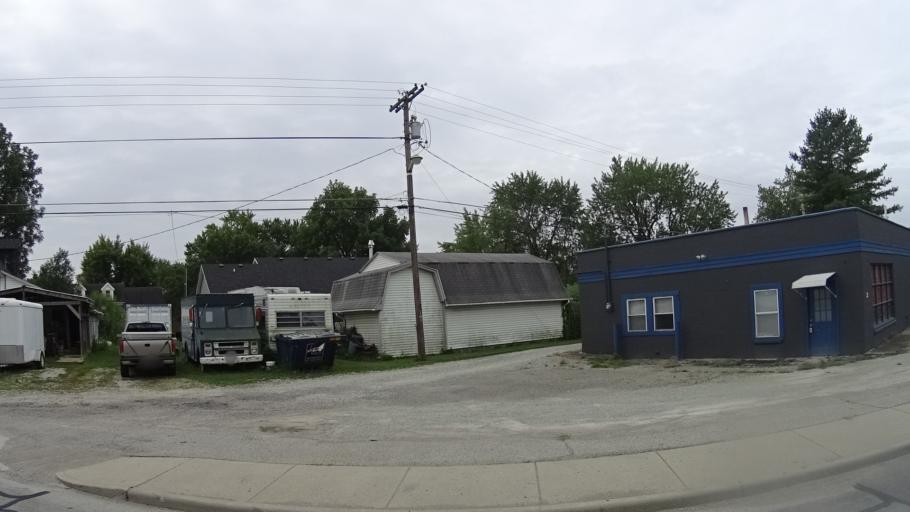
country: US
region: Indiana
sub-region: Madison County
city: Lapel
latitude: 40.0682
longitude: -85.8515
